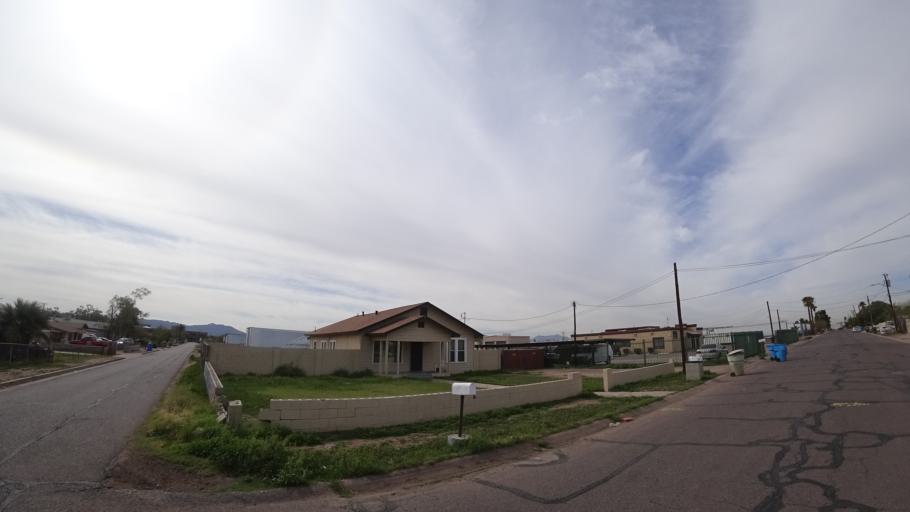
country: US
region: Arizona
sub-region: Maricopa County
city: Phoenix
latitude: 33.4332
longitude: -112.1216
